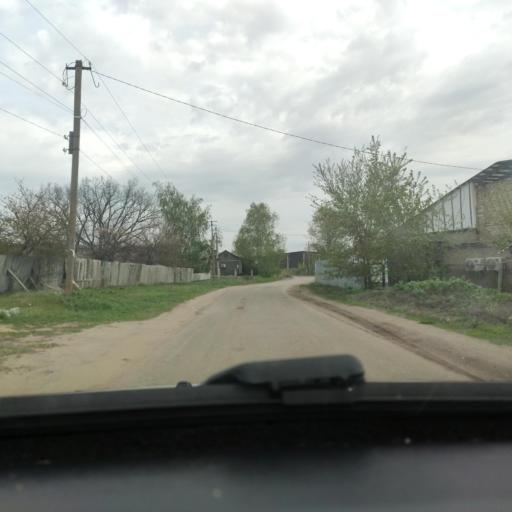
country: RU
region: Voronezj
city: Pridonskoy
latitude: 51.7326
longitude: 39.0584
